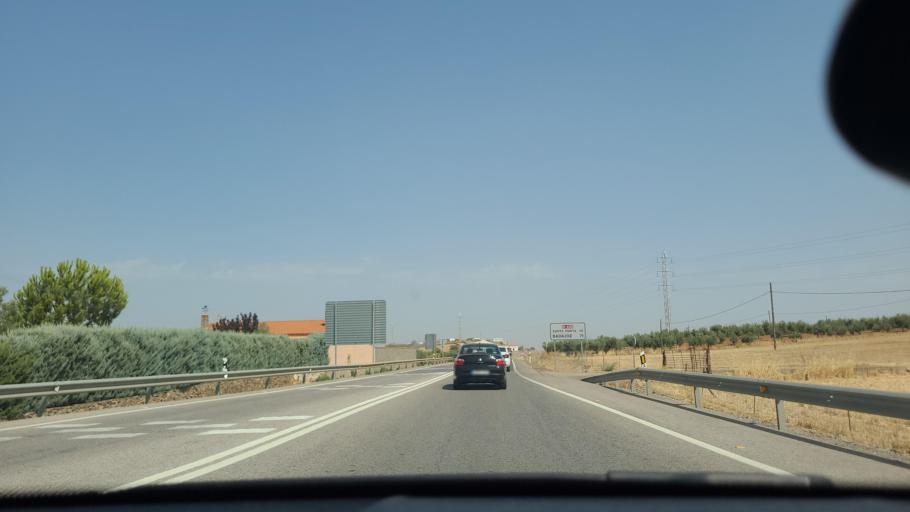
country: ES
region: Extremadura
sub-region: Provincia de Badajoz
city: Zafra
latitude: 38.4401
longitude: -6.4244
